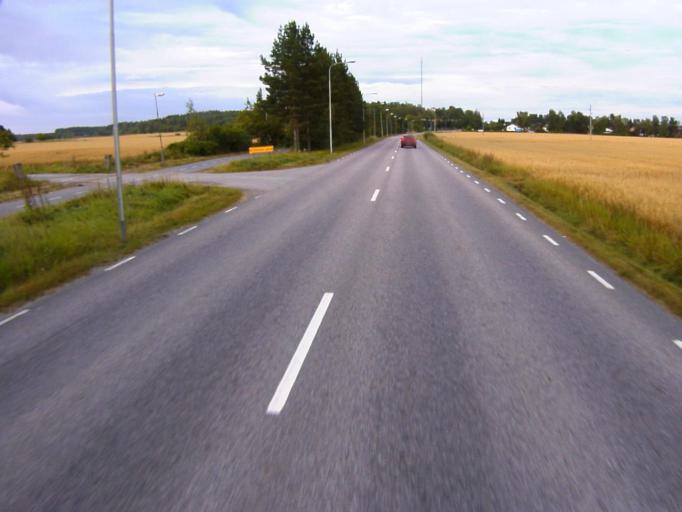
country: SE
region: Soedermanland
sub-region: Eskilstuna Kommun
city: Torshalla
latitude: 59.4043
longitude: 16.4838
